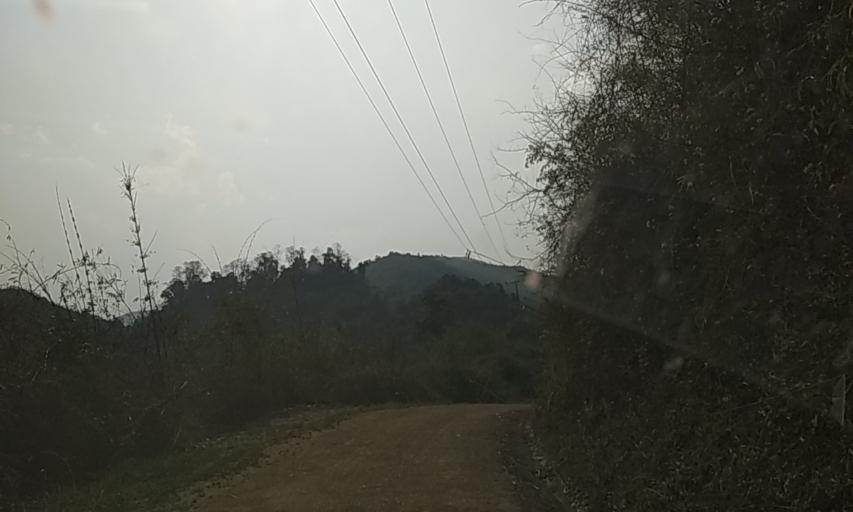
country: LA
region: Louangphabang
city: Louangphabang
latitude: 20.0458
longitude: 101.8441
